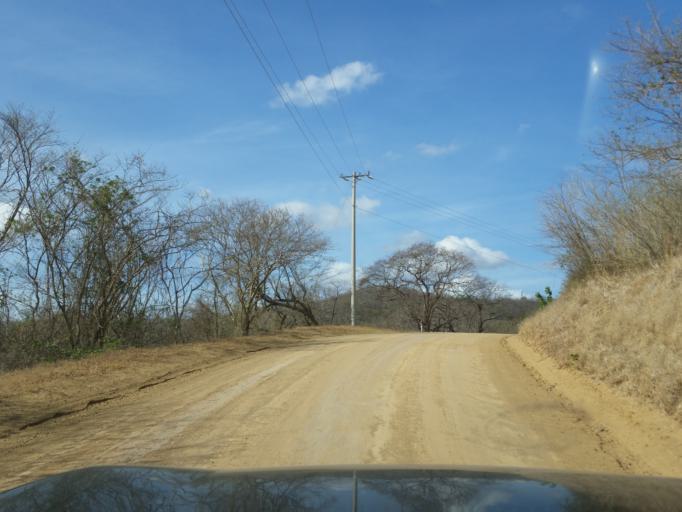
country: NI
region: Rivas
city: Tola
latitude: 11.4443
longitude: -86.0807
